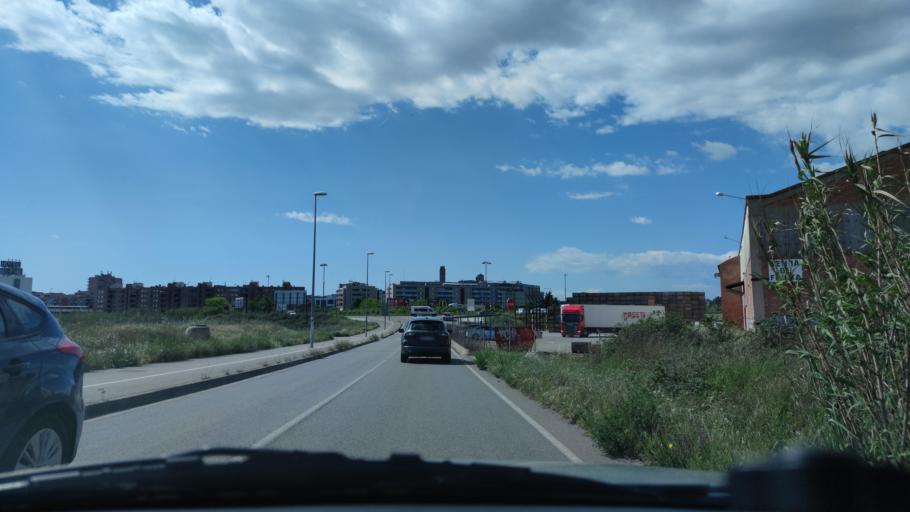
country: ES
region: Catalonia
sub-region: Provincia de Lleida
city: Lleida
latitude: 41.6095
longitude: 0.6420
